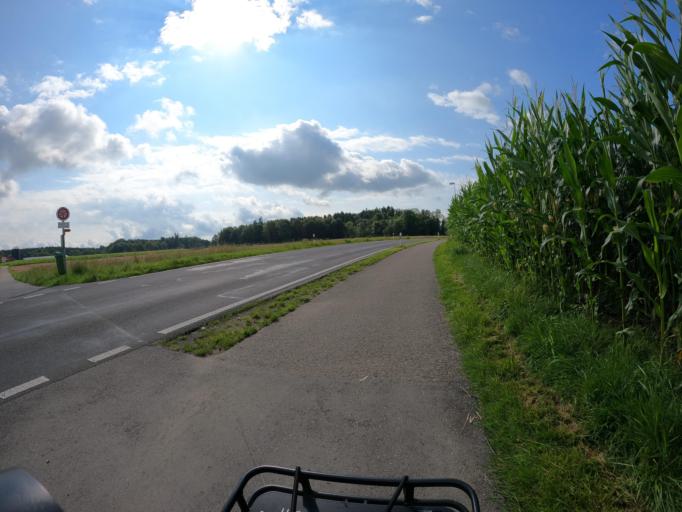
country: CH
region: Lucerne
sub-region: Hochdorf District
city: Hochdorf
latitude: 47.1578
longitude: 8.2925
